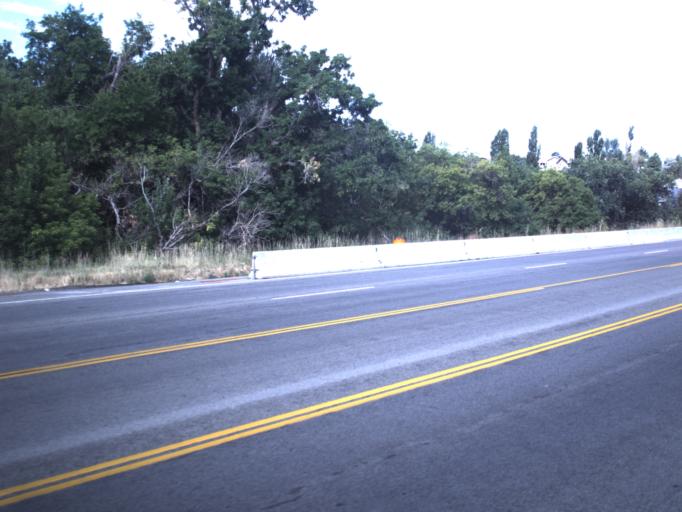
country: US
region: Utah
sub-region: Weber County
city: Uintah
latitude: 41.1596
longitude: -111.9454
